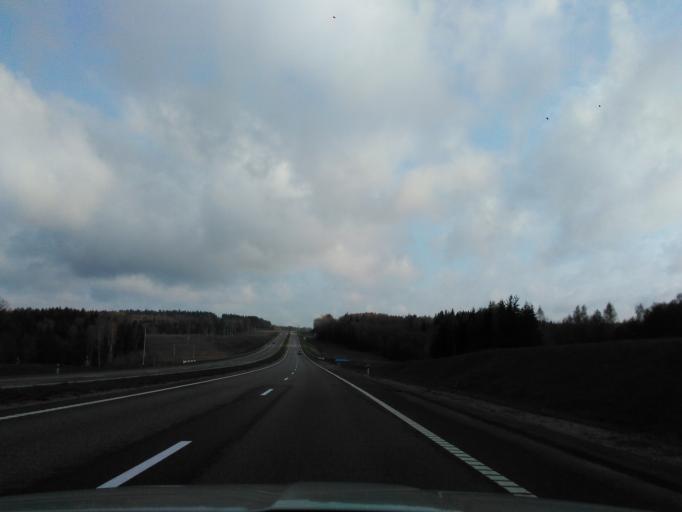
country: BY
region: Minsk
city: Lahoysk
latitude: 54.1887
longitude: 27.8158
